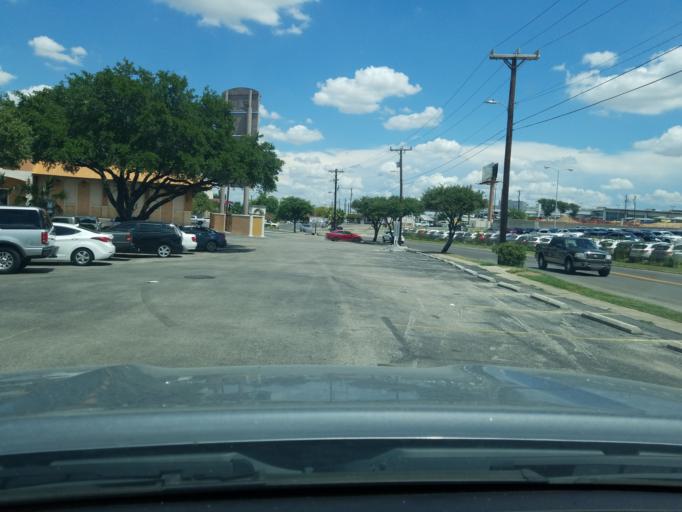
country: US
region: Texas
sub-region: Bexar County
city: Castle Hills
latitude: 29.5291
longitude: -98.4999
